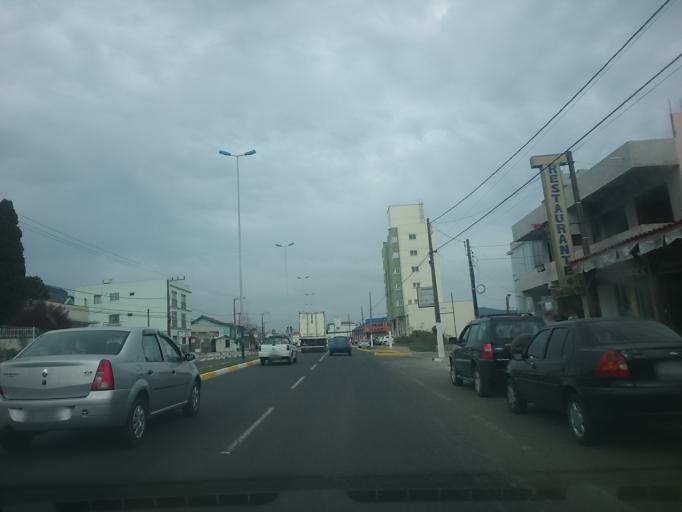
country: BR
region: Santa Catarina
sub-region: Lages
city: Lages
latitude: -27.8263
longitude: -50.3269
